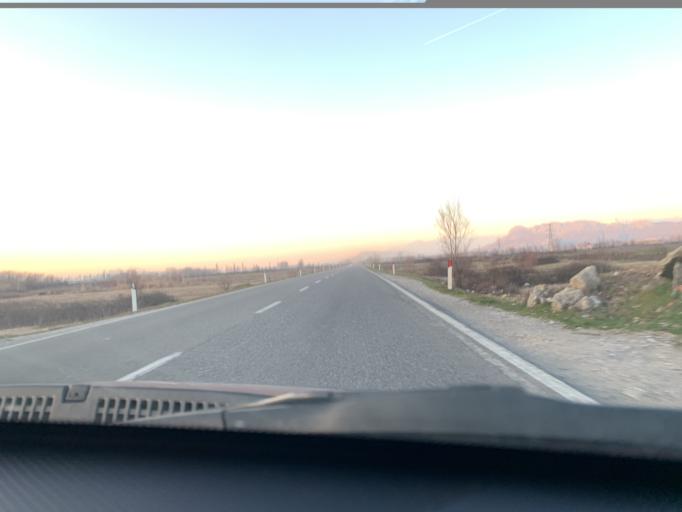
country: AL
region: Lezhe
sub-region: Rrethi i Lezhes
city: Balldreni i Ri
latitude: 41.8445
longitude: 19.6432
